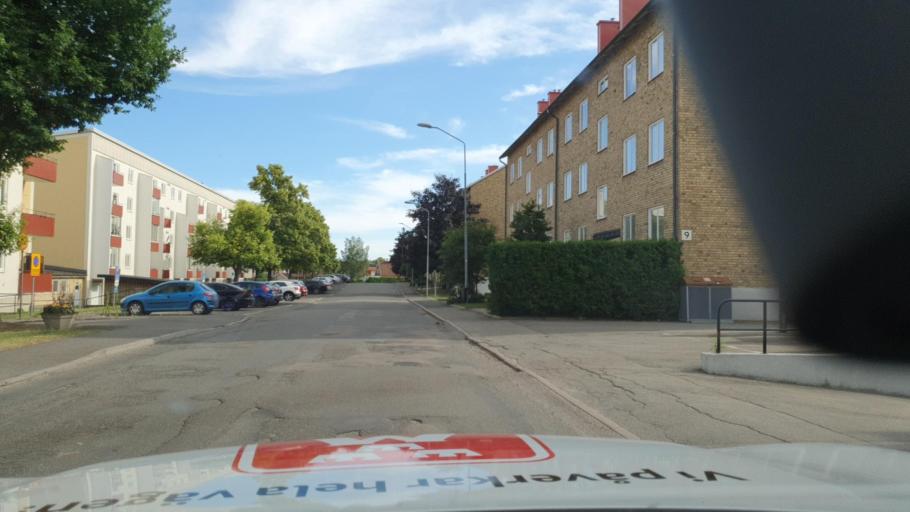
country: SE
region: Vaestra Goetaland
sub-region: Skovde Kommun
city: Skoevde
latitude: 58.3883
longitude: 13.8689
